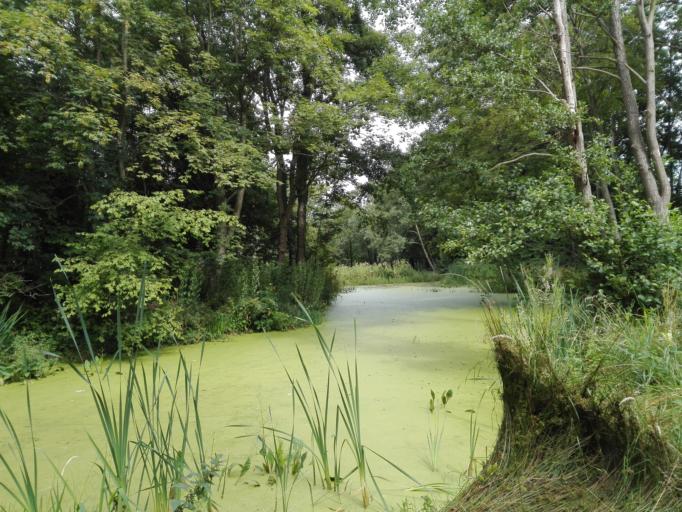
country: DK
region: Central Jutland
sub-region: Arhus Kommune
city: Beder
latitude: 56.0449
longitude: 10.2577
